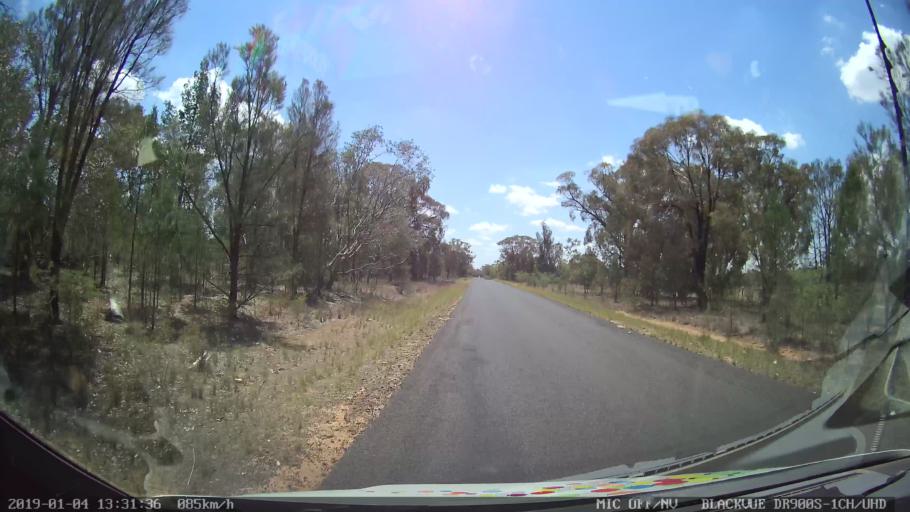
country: AU
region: New South Wales
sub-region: Parkes
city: Peak Hill
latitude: -32.6205
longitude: 148.5488
